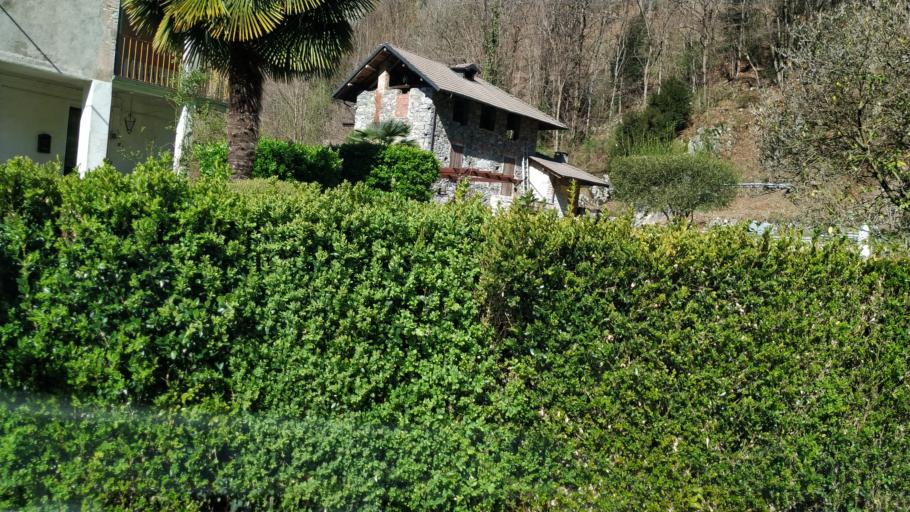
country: IT
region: Piedmont
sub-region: Provincia di Vercelli
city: Civiasco
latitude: 45.7947
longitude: 8.2789
